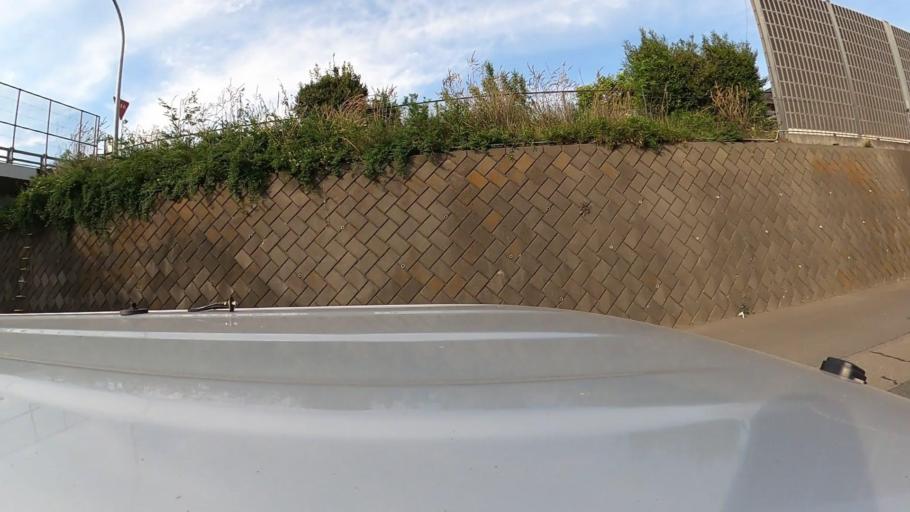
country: JP
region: Saitama
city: Oi
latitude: 35.8273
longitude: 139.5125
